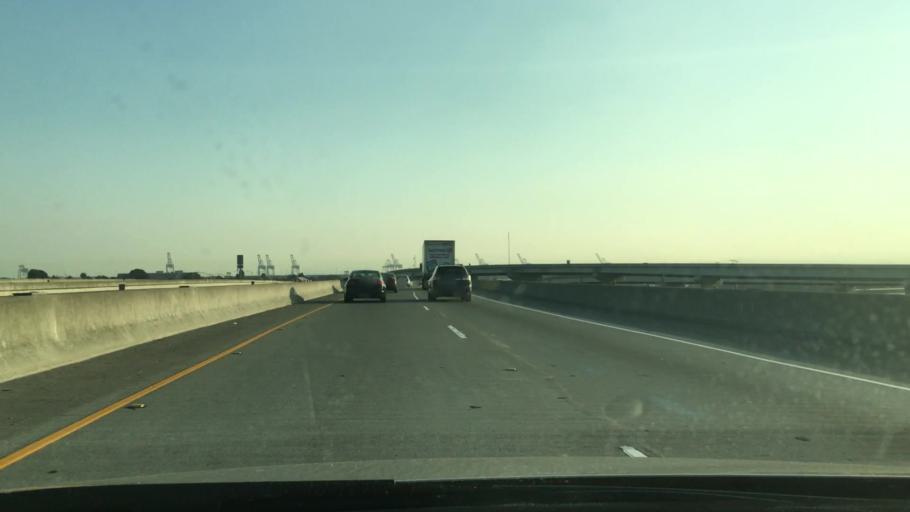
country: US
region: California
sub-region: Alameda County
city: Emeryville
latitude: 37.8210
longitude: -122.2933
